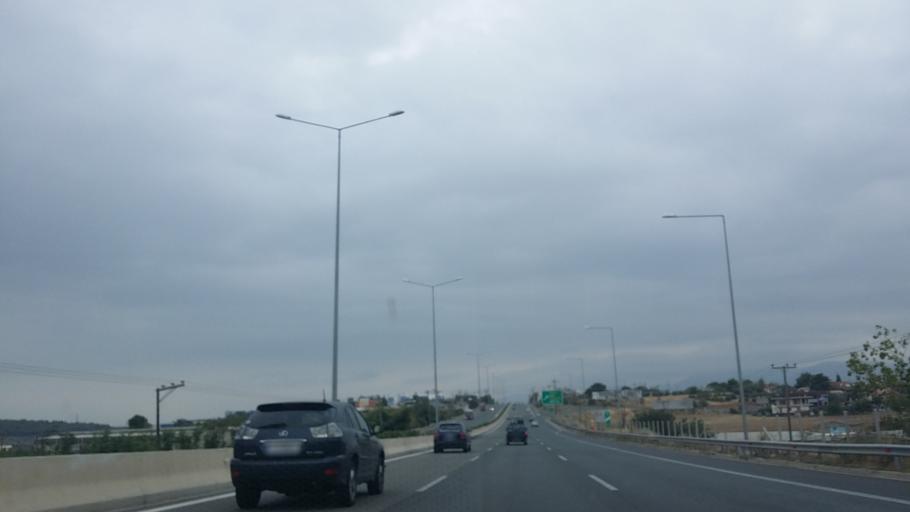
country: GR
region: Central Greece
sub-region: Nomos Voiotias
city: Oinofyta
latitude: 38.3287
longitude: 23.6065
